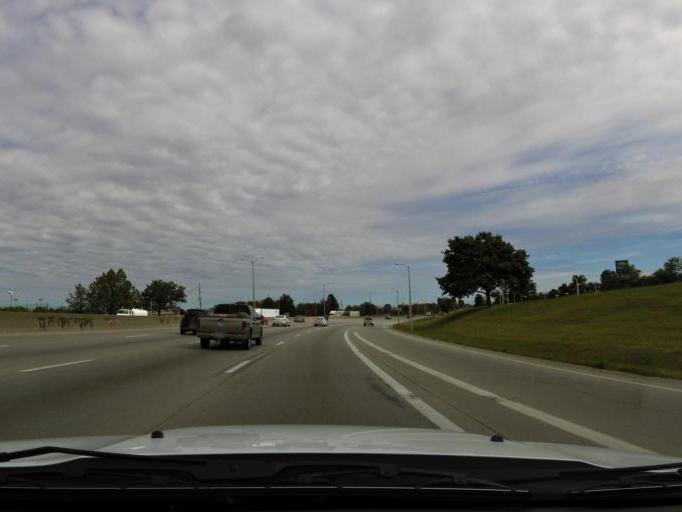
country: US
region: Kentucky
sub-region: Boone County
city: Florence
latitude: 39.0024
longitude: -84.6468
